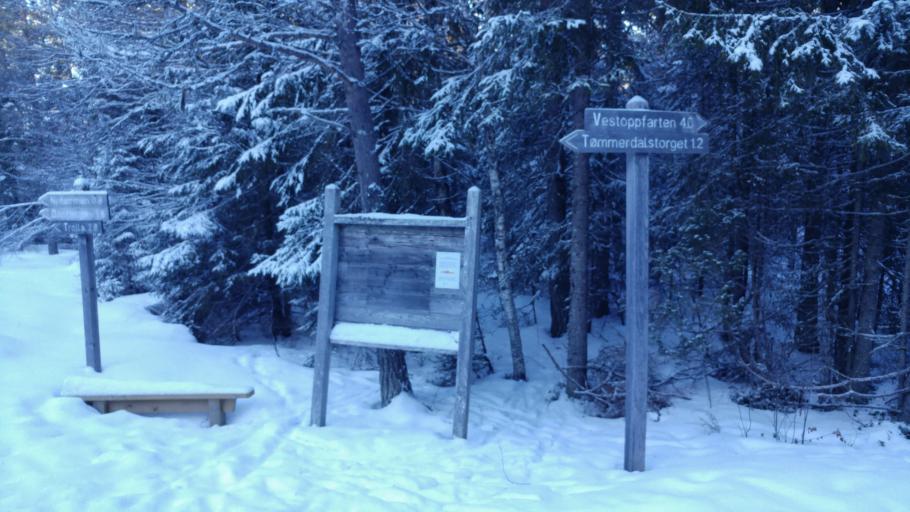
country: NO
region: Sor-Trondelag
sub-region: Trondheim
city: Trondheim
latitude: 63.4358
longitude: 10.2942
